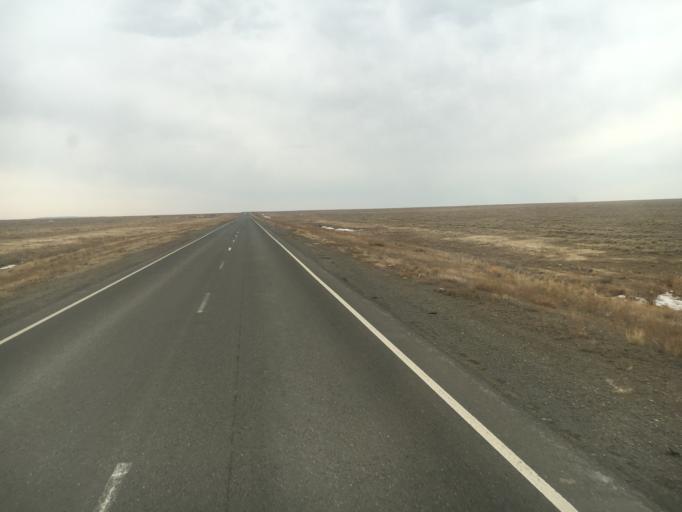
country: KZ
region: Aqtoebe
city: Yrghyz
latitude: 48.7113
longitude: 60.8374
